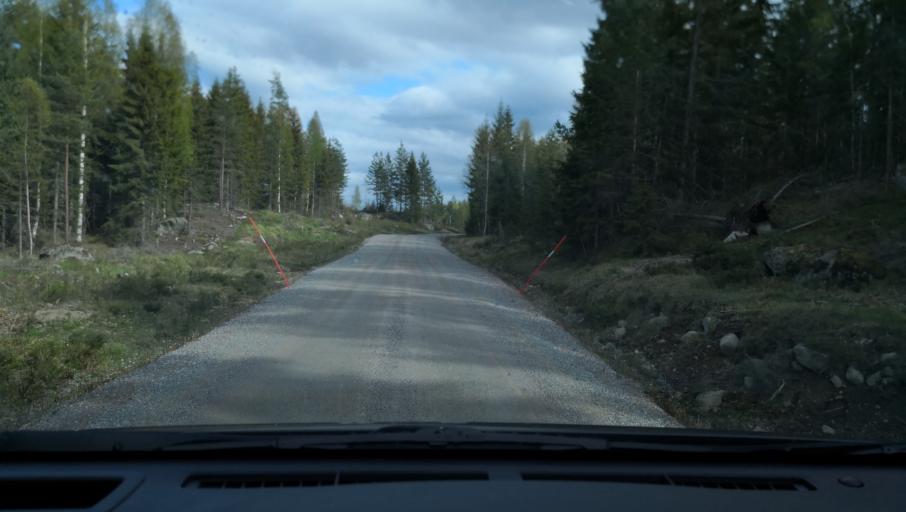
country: SE
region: Vaestmanland
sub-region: Fagersta Kommun
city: Fagersta
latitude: 60.1591
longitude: 15.7055
